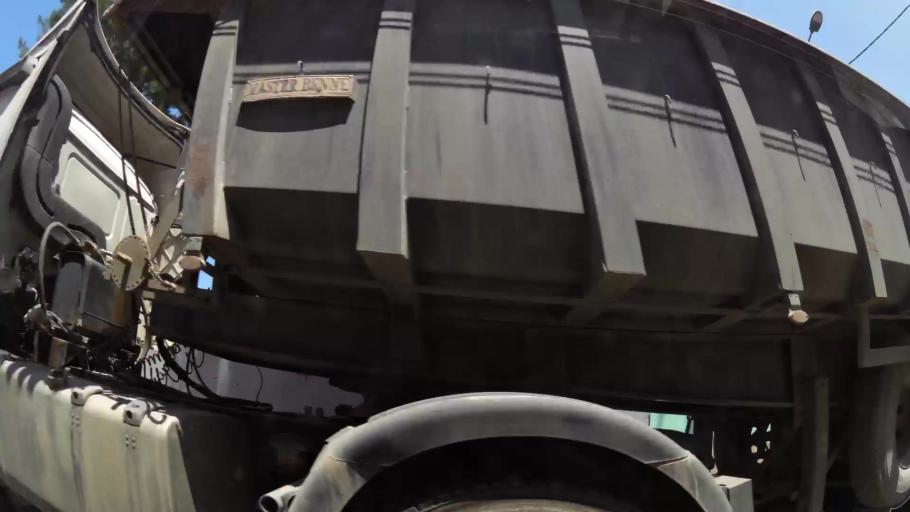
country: MA
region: Gharb-Chrarda-Beni Hssen
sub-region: Kenitra Province
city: Kenitra
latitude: 34.2629
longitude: -6.6212
